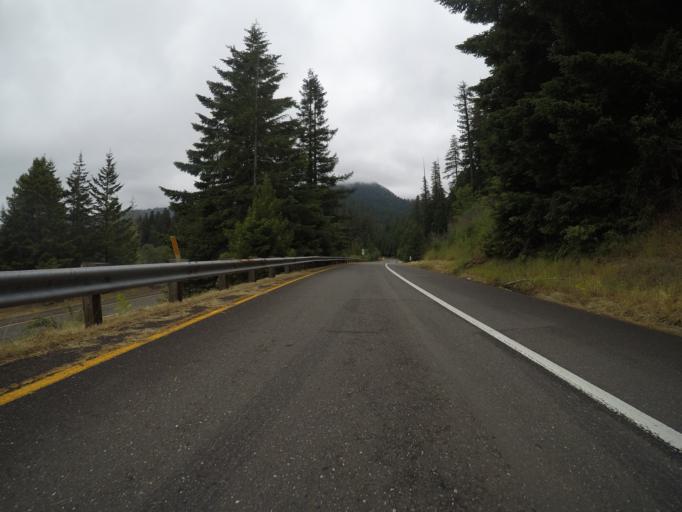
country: US
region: California
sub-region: Humboldt County
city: Rio Dell
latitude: 40.4466
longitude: -124.0399
